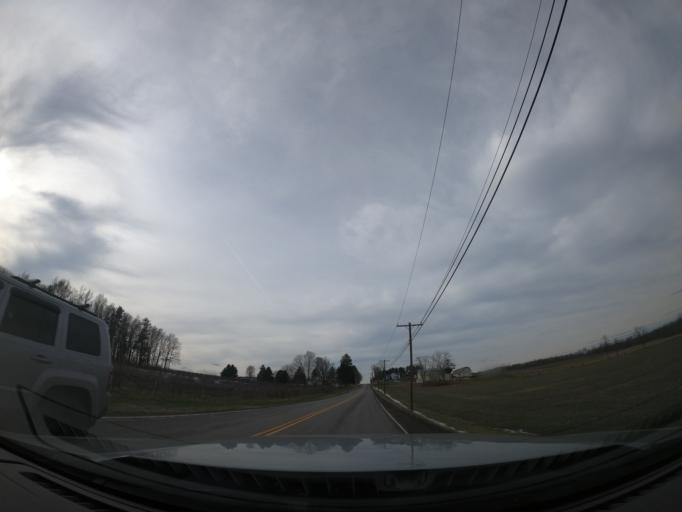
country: US
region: New York
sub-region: Yates County
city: Dundee
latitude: 42.5005
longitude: -76.9278
